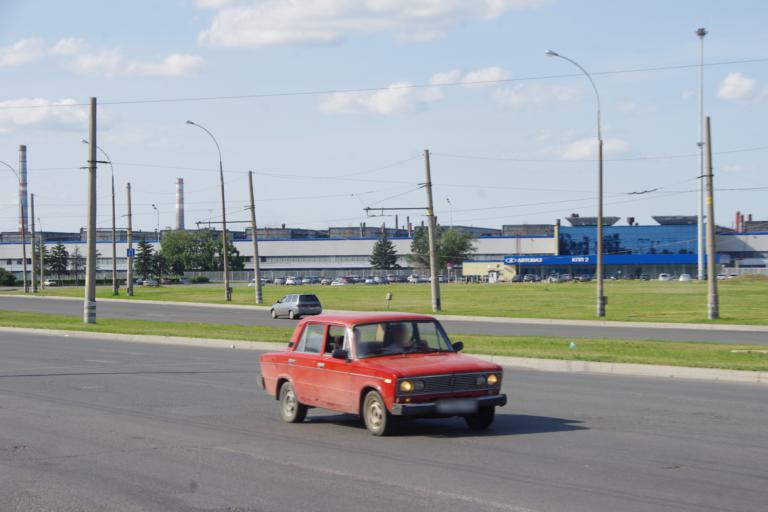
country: RU
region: Samara
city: Tol'yatti
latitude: 53.5534
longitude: 49.2605
